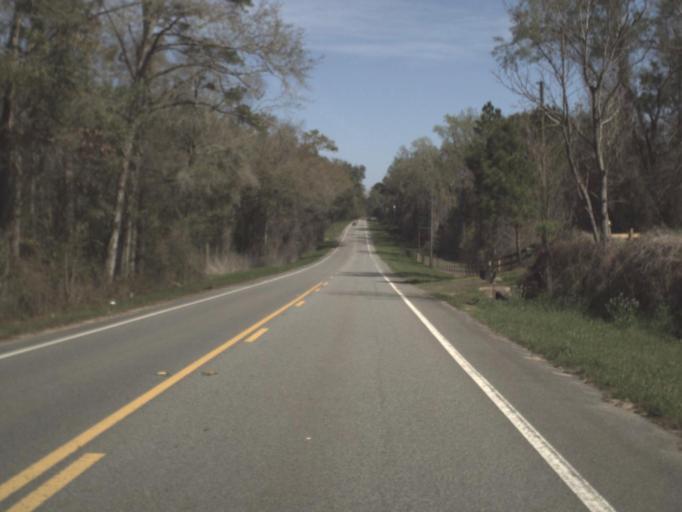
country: US
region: Florida
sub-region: Jefferson County
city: Monticello
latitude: 30.5172
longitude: -84.0243
